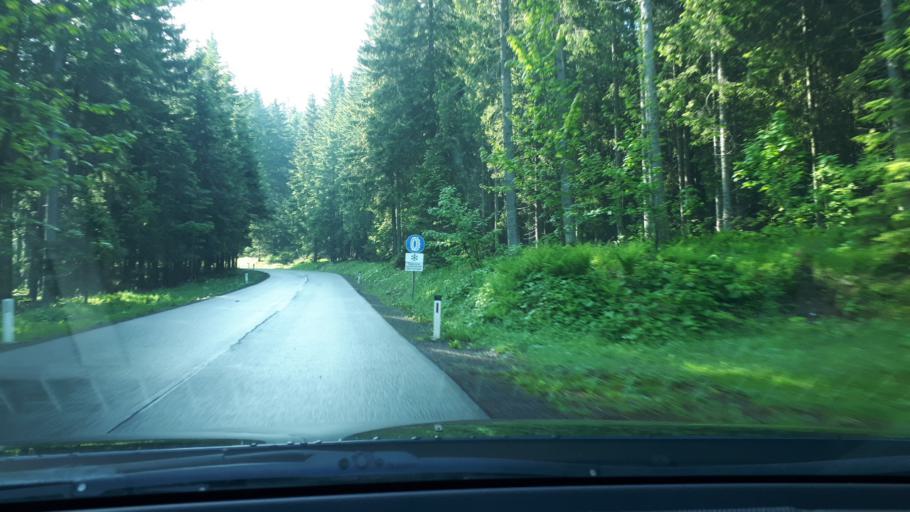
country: AT
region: Styria
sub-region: Politischer Bezirk Voitsberg
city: Modriach
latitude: 46.9273
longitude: 15.0099
